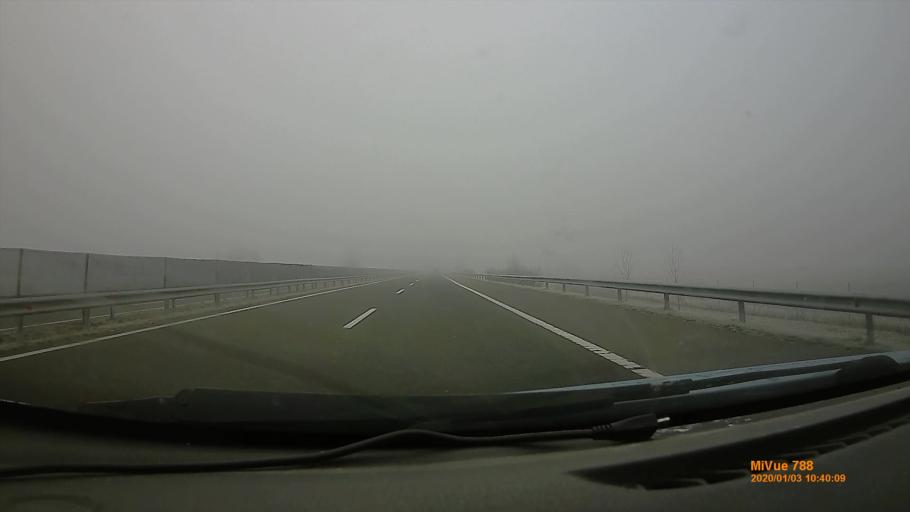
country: HU
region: Tolna
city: Bataszek
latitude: 46.2375
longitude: 18.7167
